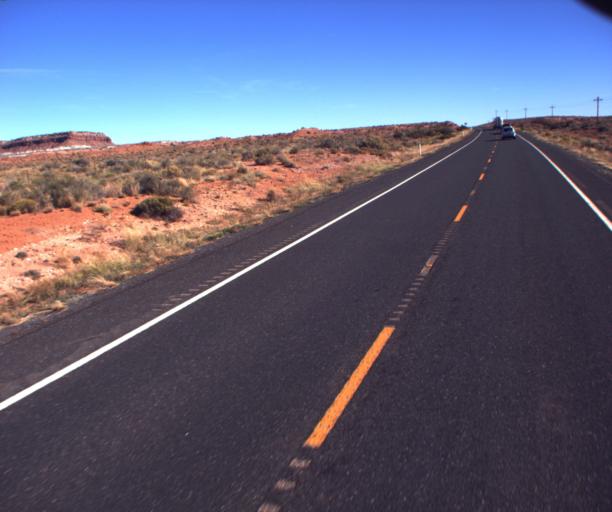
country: US
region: Arizona
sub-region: Coconino County
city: Fredonia
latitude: 36.9003
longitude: -112.6005
